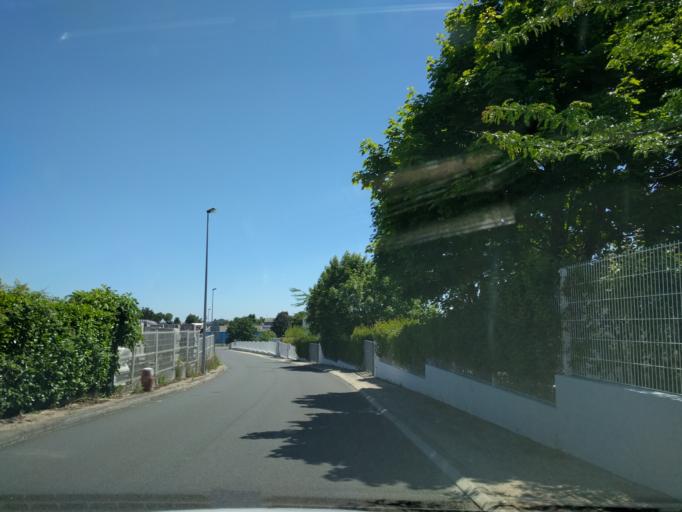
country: FR
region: Poitou-Charentes
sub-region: Departement des Deux-Sevres
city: Niort
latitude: 46.3357
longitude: -0.4200
